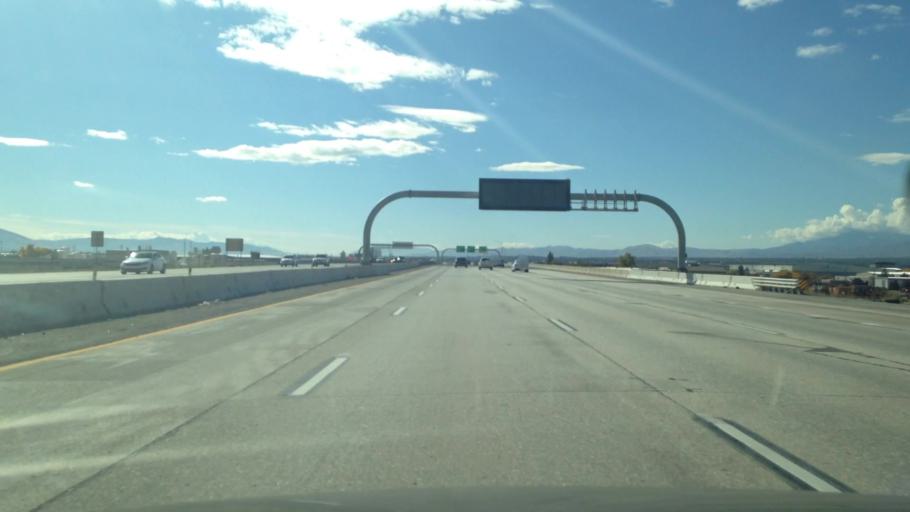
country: US
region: Utah
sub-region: Salt Lake County
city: Salt Lake City
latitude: 40.7492
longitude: -111.9488
